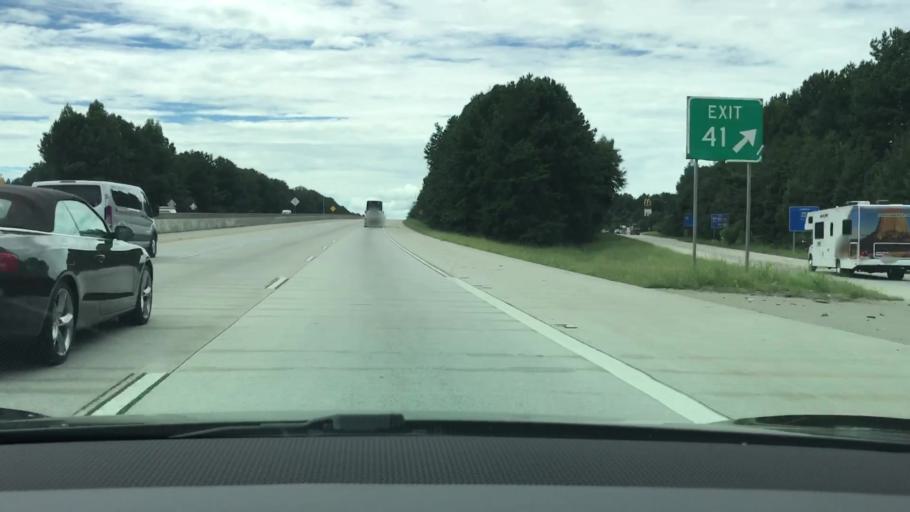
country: US
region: Georgia
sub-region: Coweta County
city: East Newnan
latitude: 33.3268
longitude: -84.7749
